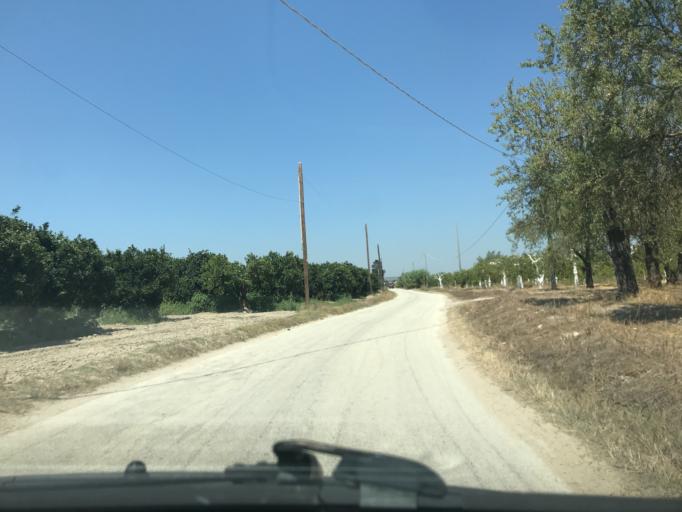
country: IT
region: Sicily
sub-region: Provincia di Siracusa
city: Noto
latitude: 36.8314
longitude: 15.0380
